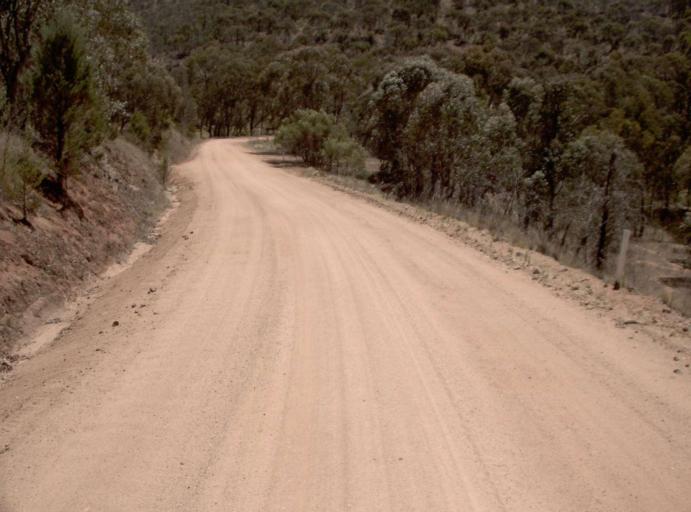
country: AU
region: New South Wales
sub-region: Snowy River
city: Jindabyne
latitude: -36.9220
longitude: 148.3922
